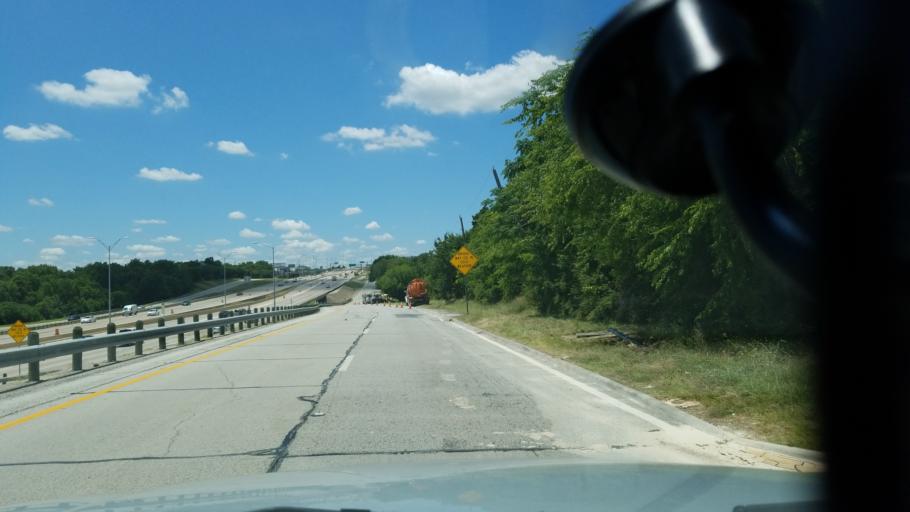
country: US
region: Texas
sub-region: Dallas County
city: Duncanville
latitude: 32.6698
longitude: -96.8637
